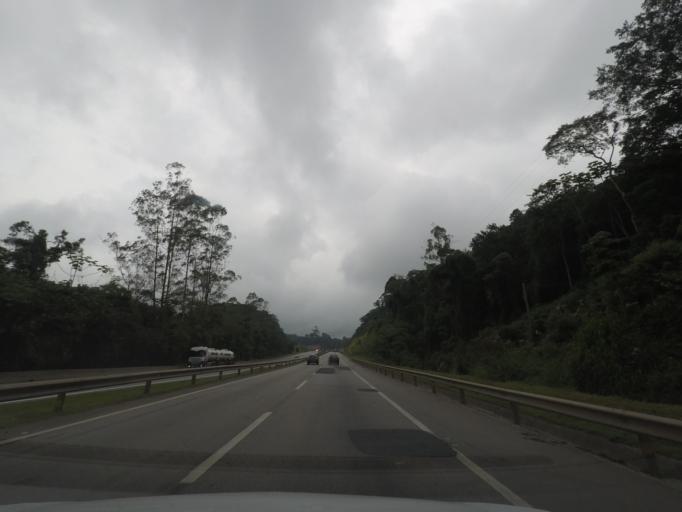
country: BR
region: Sao Paulo
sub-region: Juquitiba
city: Juquitiba
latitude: -24.0344
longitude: -47.1850
